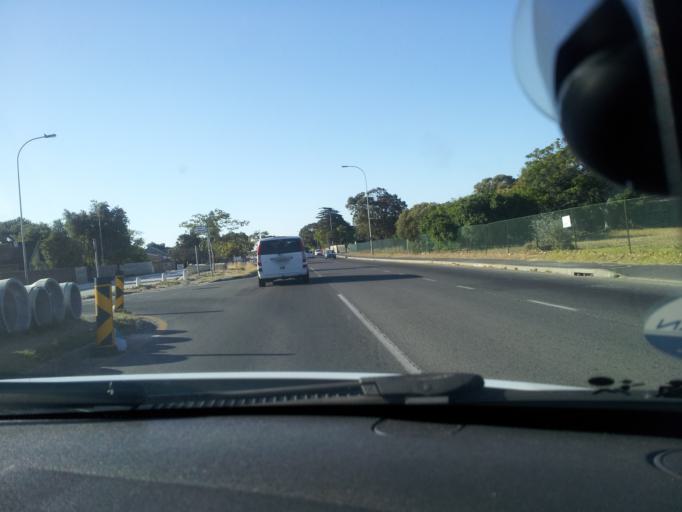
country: ZA
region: Western Cape
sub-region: Cape Winelands District Municipality
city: Stellenbosch
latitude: -34.1065
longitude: 18.8369
